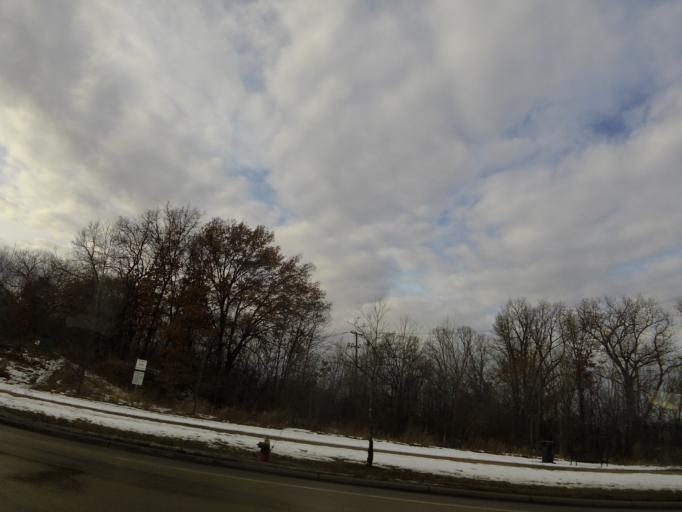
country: US
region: Minnesota
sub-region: Ramsey County
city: Saint Paul
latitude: 44.9699
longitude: -93.0487
